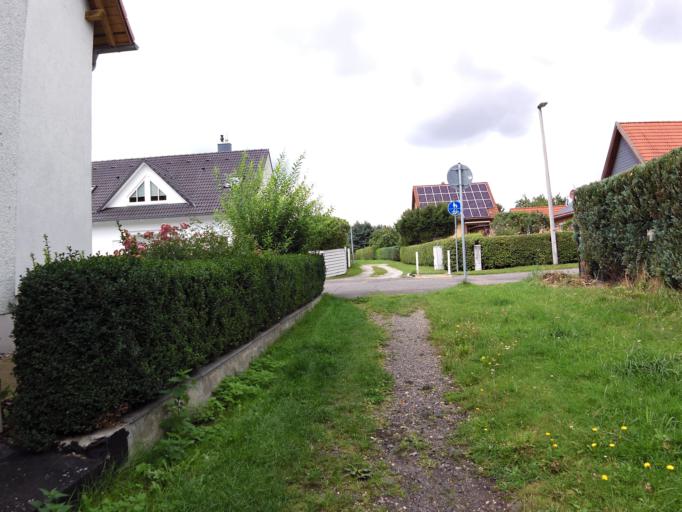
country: DE
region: Saxony
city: Rackwitz
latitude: 51.3846
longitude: 12.4172
